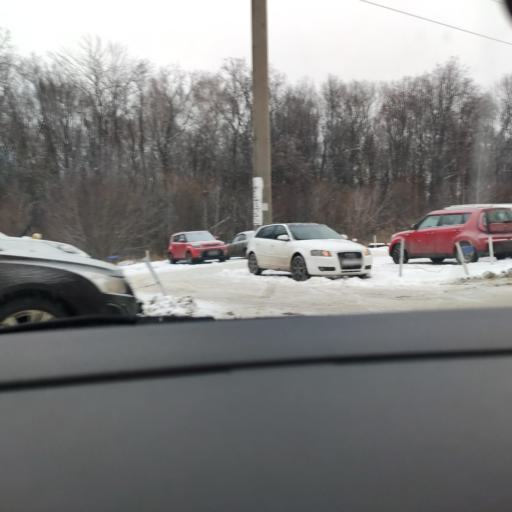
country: RU
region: Voronezj
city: Podgornoye
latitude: 51.7323
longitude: 39.2026
